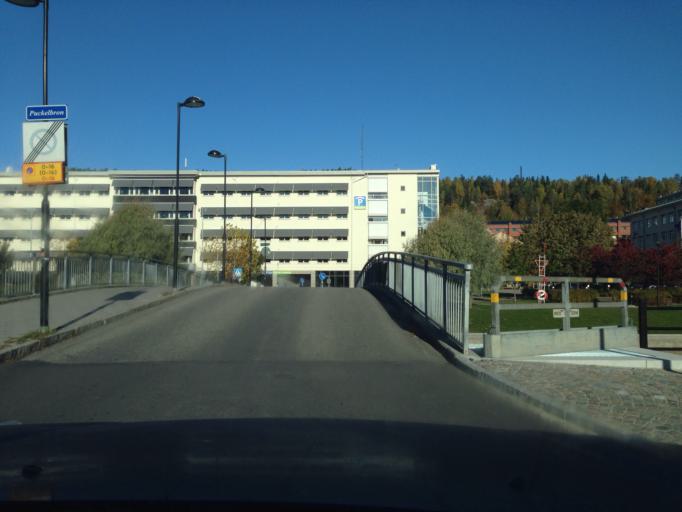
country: SE
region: Vaesternorrland
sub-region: Sundsvalls Kommun
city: Sundsvall
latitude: 62.3924
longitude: 17.3072
